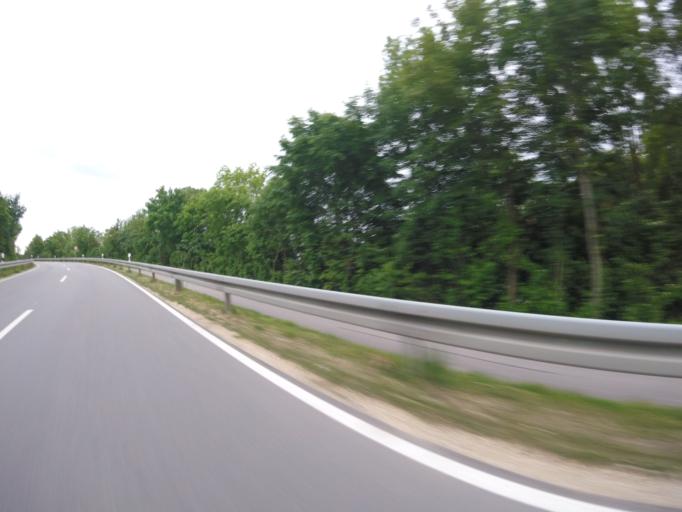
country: DE
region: Bavaria
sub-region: Upper Bavaria
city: Eching
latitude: 48.2955
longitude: 11.6314
